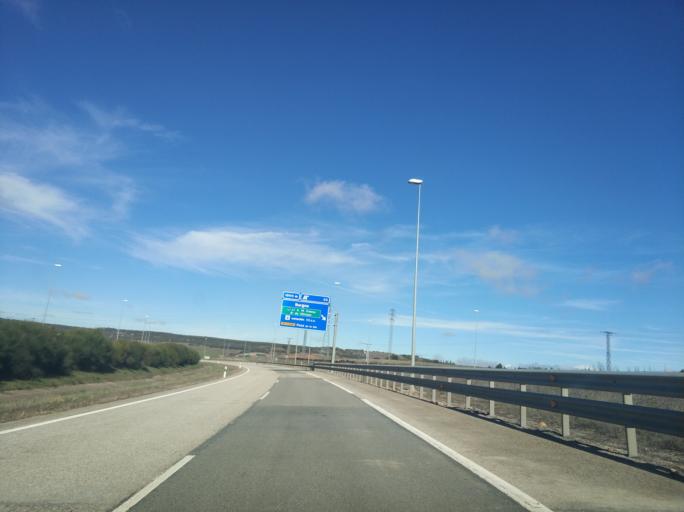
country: ES
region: Castille and Leon
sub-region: Provincia de Burgos
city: Burgos
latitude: 42.3725
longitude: -3.6418
